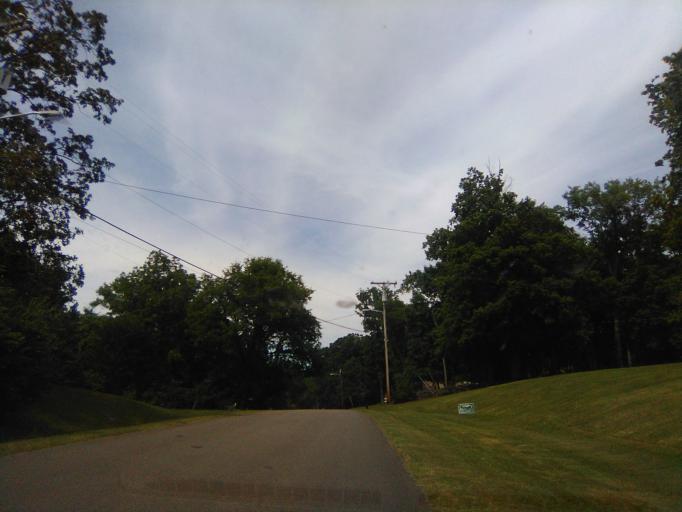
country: US
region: Tennessee
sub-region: Davidson County
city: Belle Meade
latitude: 36.1230
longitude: -86.8952
